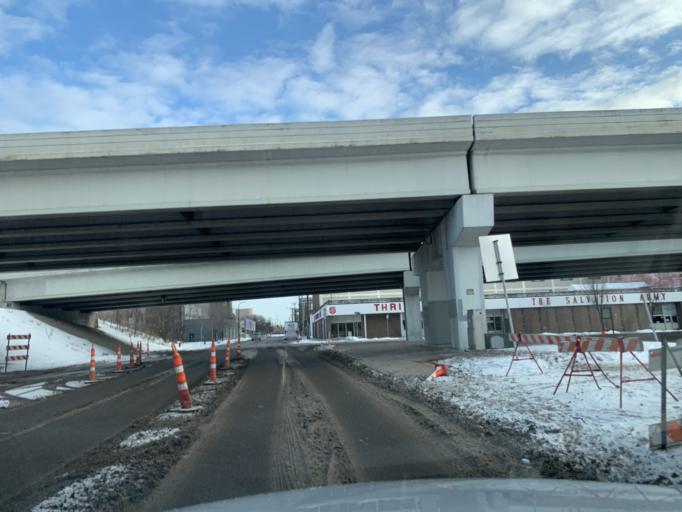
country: US
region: Minnesota
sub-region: Hennepin County
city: Minneapolis
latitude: 44.9883
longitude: -93.2834
